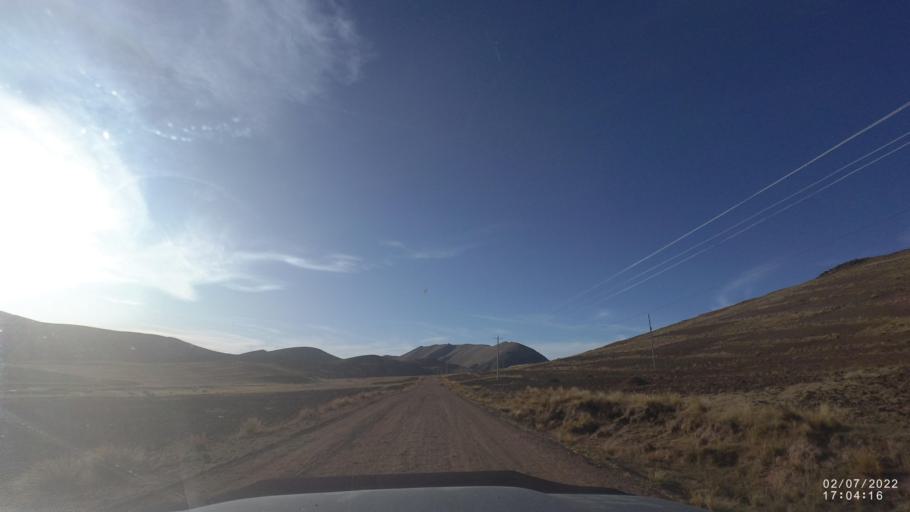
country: BO
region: Cochabamba
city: Irpa Irpa
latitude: -17.9167
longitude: -66.5584
